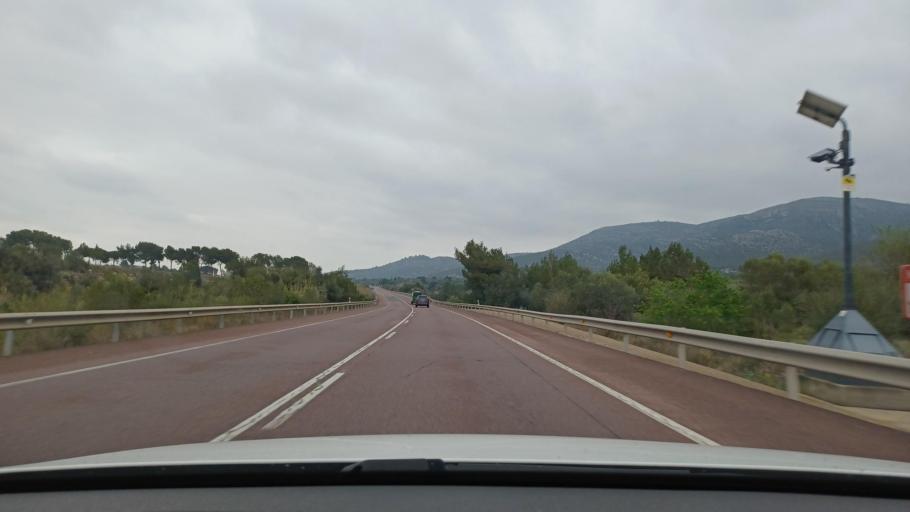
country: ES
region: Valencia
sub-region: Provincia de Castello
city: Santa Magdalena de Pulpis
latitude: 40.3653
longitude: 0.3159
